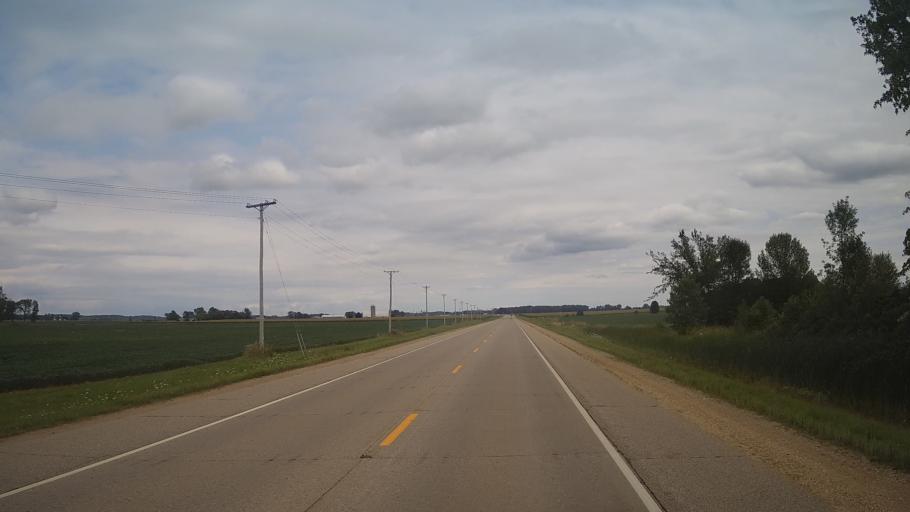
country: US
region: Wisconsin
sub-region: Waushara County
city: Redgranite
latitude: 44.0375
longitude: -89.0613
